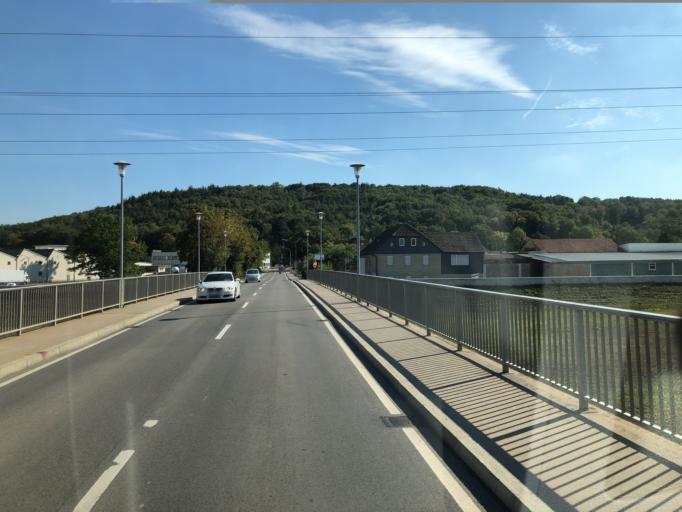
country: DE
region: Bavaria
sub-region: Upper Franconia
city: Michelau
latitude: 50.1580
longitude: 11.1153
